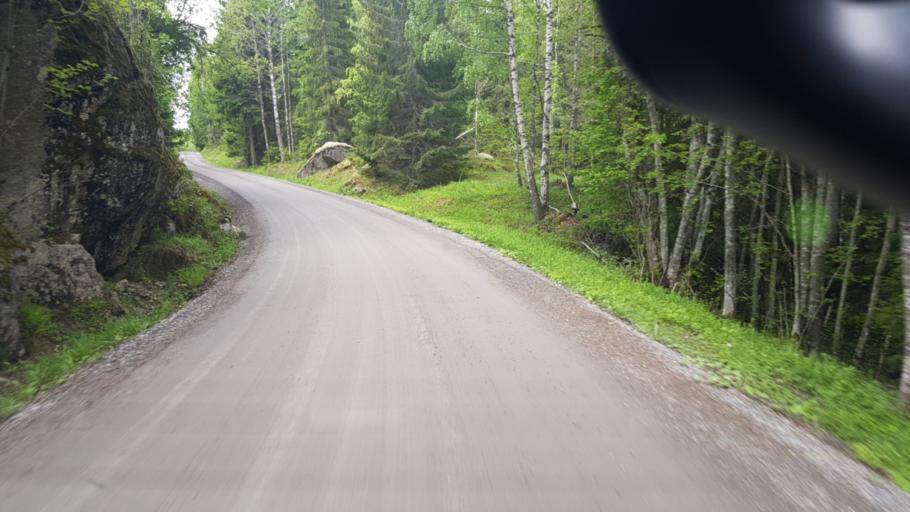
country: NO
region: Ostfold
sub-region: Romskog
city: Romskog
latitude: 59.7168
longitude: 11.9878
